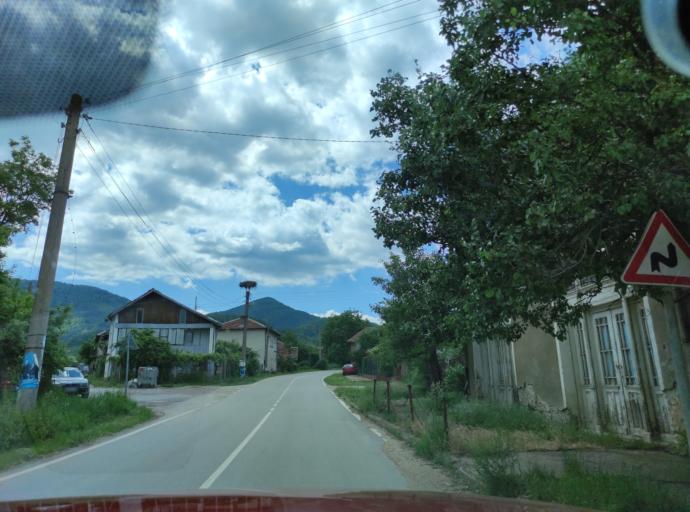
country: BG
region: Montana
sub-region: Obshtina Chiprovtsi
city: Chiprovtsi
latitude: 43.4687
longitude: 22.8571
